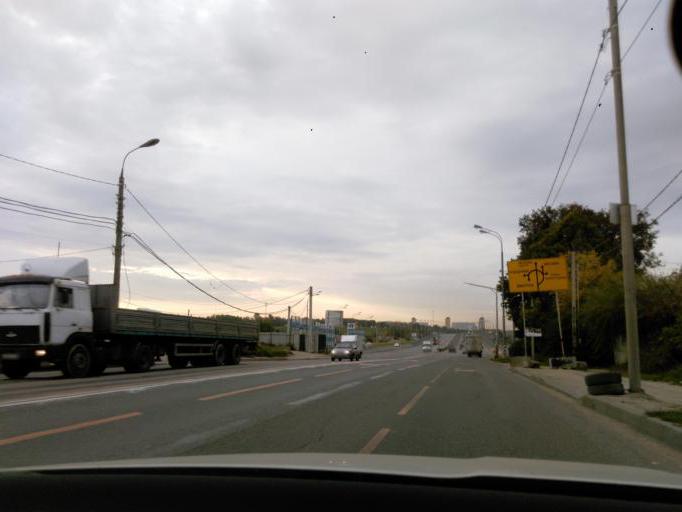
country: RU
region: Moscow
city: Severnyy
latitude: 55.9546
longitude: 37.5362
